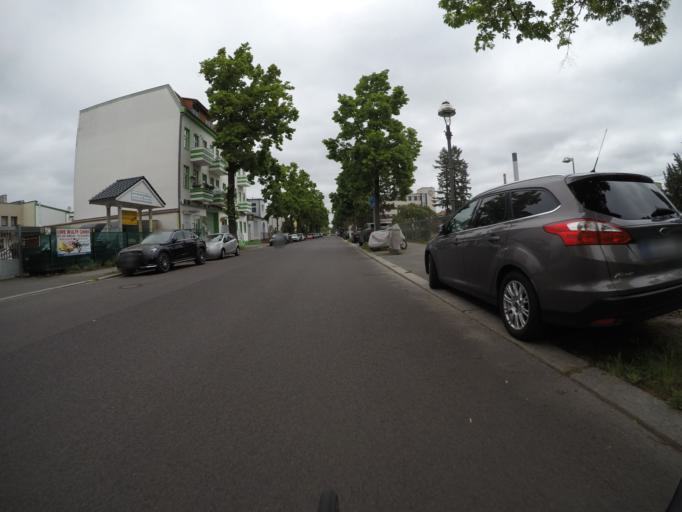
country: DE
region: Berlin
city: Wittenau
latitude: 52.6007
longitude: 13.3336
